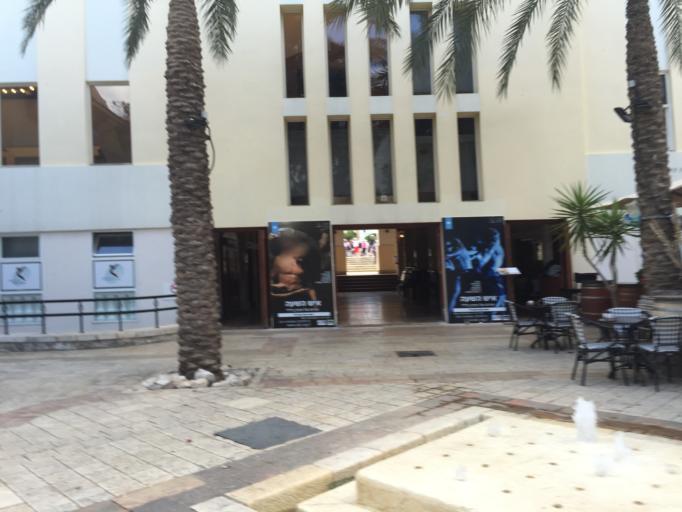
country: IL
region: Tel Aviv
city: Yafo
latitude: 32.0610
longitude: 34.7642
